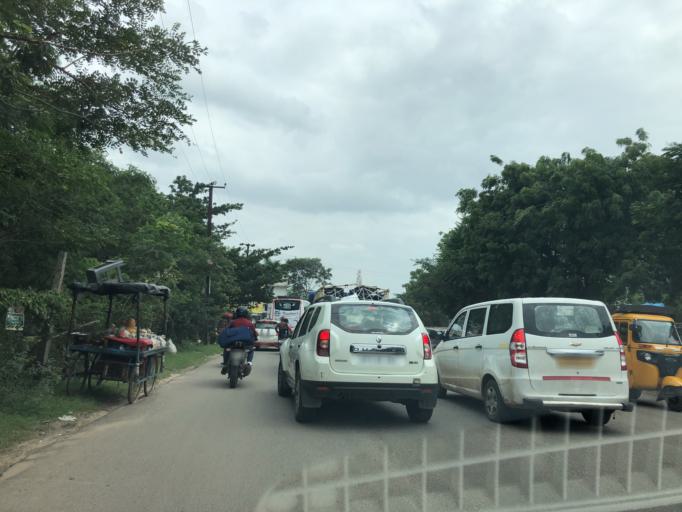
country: IN
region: Telangana
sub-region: Rangareddi
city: Quthbullapur
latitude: 17.4711
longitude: 78.4760
